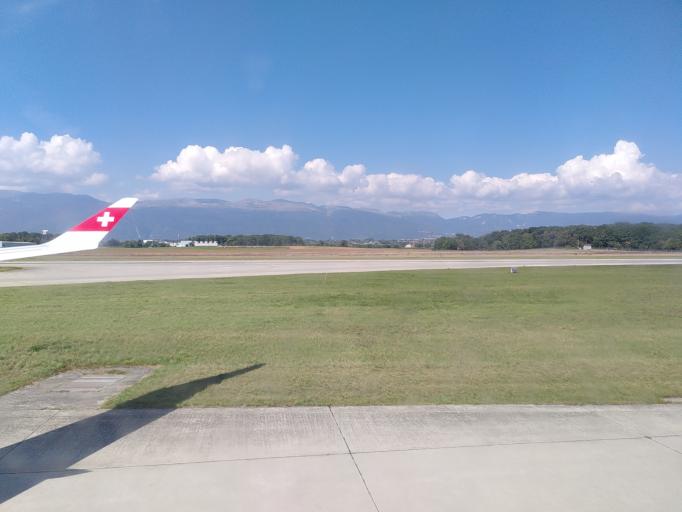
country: CH
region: Geneva
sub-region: Geneva
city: Les Avanchets
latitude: 46.2356
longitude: 6.1085
